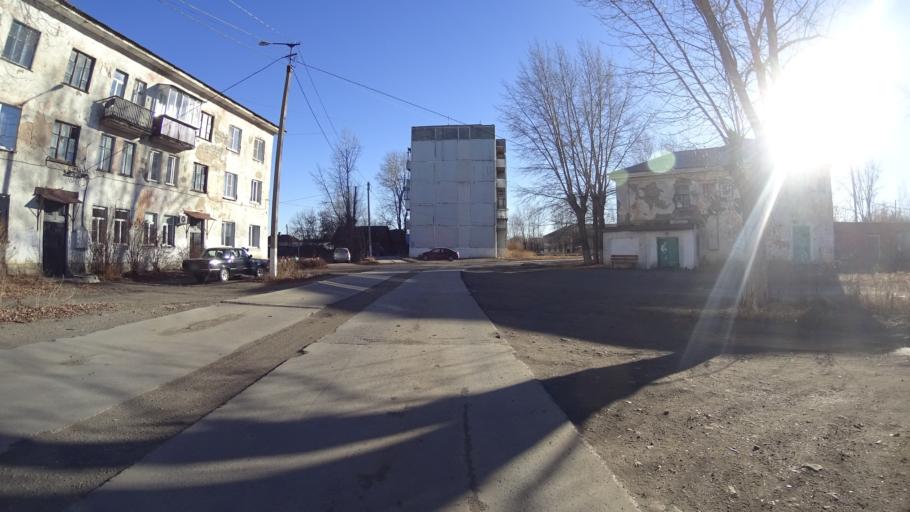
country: RU
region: Chelyabinsk
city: Troitsk
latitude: 54.1088
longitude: 61.5541
